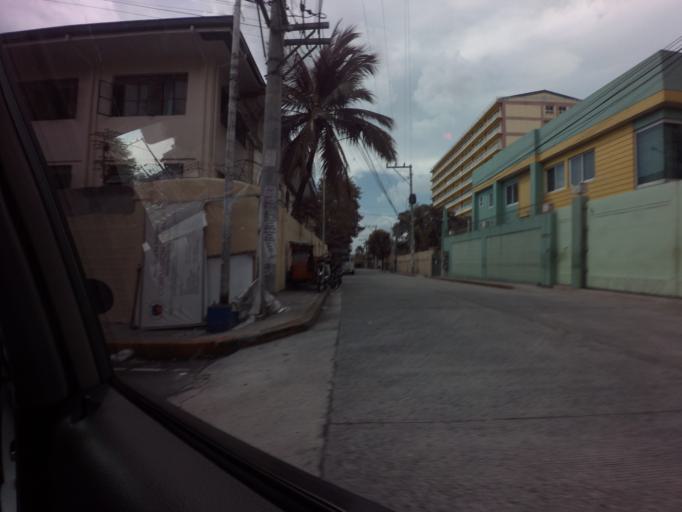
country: PH
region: Metro Manila
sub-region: San Juan
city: San Juan
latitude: 14.6032
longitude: 121.0124
